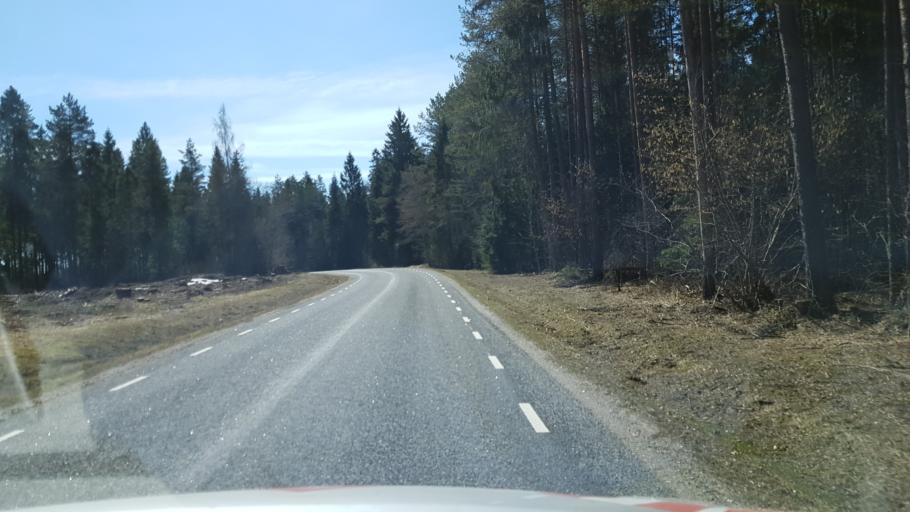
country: EE
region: Laeaene-Virumaa
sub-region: Vinni vald
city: Vinni
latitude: 59.1278
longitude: 26.5214
